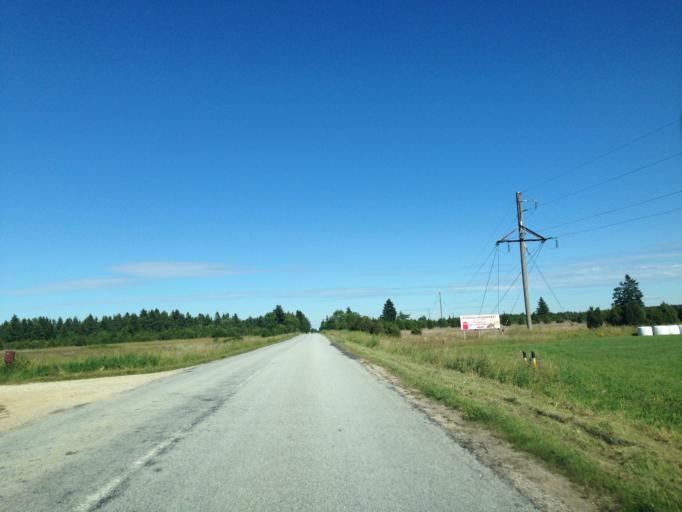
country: EE
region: Harju
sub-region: Raasiku vald
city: Raasiku
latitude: 59.4685
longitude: 25.2635
